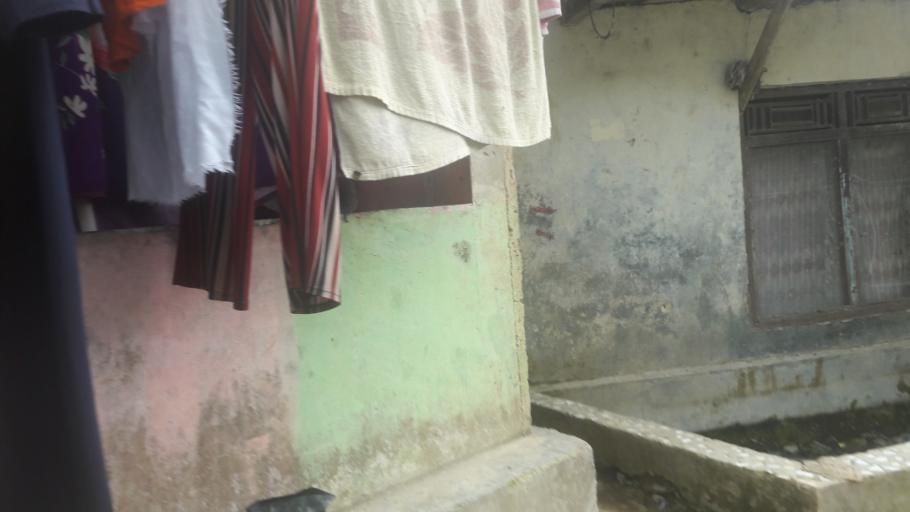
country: ID
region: West Java
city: Cipeundeuy
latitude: -6.6669
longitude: 106.5356
